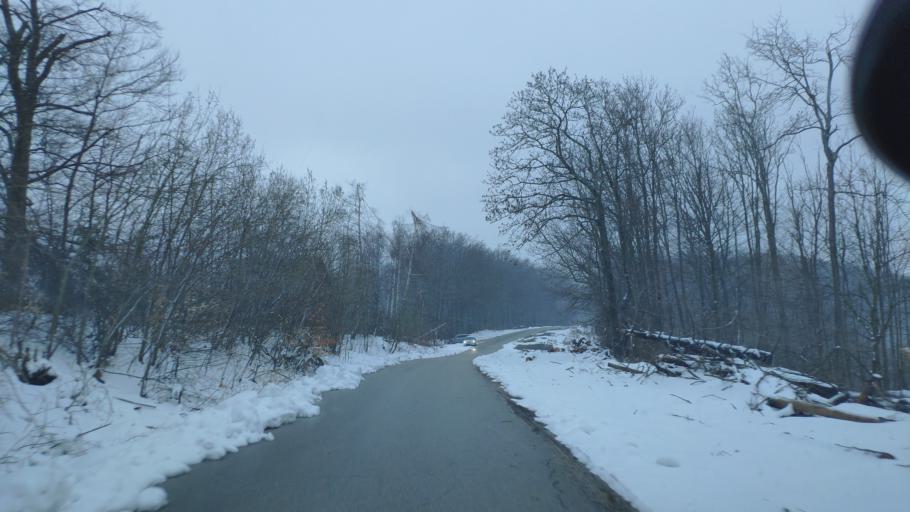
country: CZ
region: Zlin
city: Strani
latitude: 48.8471
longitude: 17.6908
